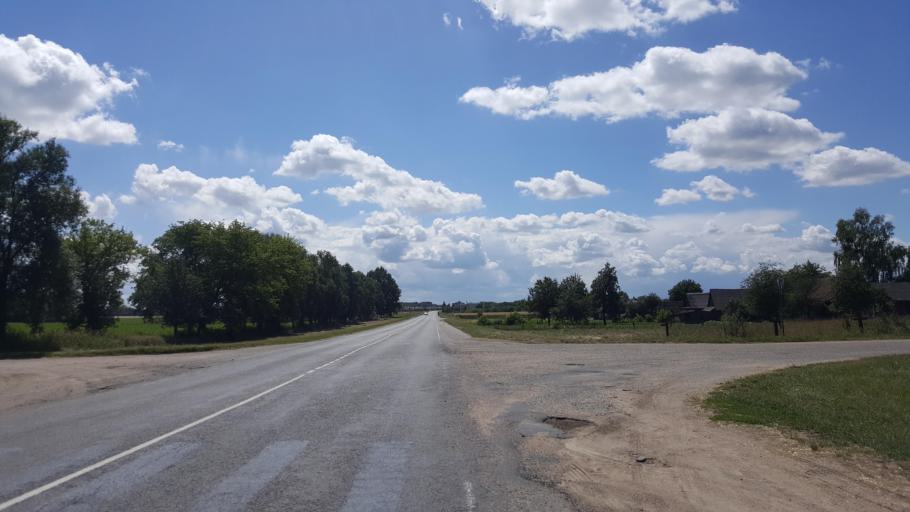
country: BY
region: Brest
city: Kamyanyets
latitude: 52.3350
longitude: 23.9114
